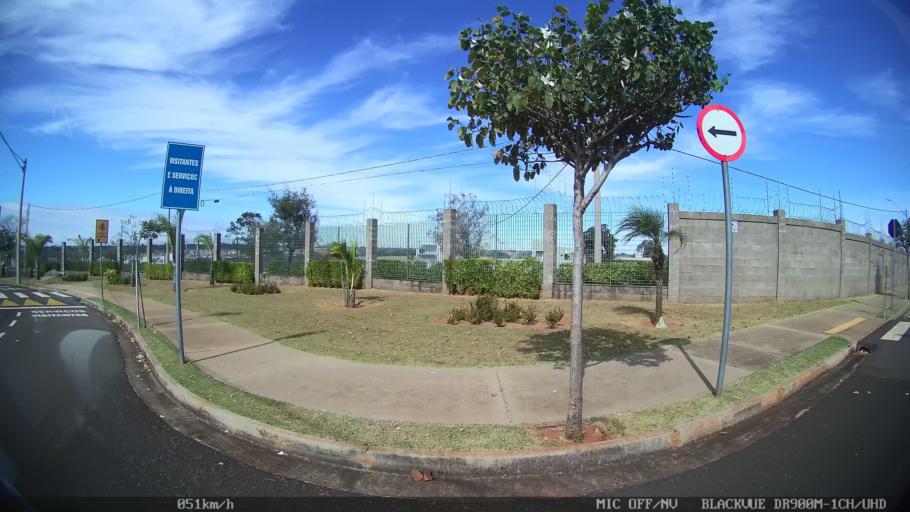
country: BR
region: Sao Paulo
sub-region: Sao Jose Do Rio Preto
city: Sao Jose do Rio Preto
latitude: -20.8522
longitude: -49.3741
